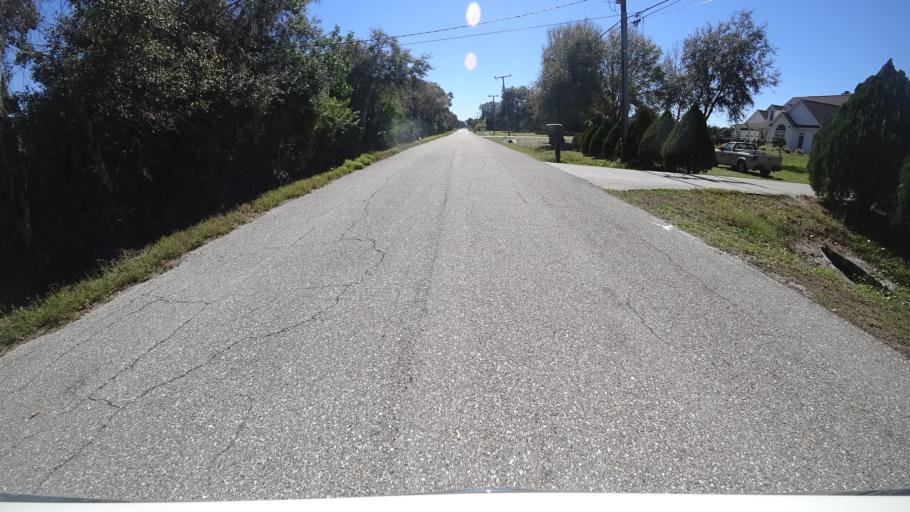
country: US
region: Florida
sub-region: Manatee County
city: Memphis
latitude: 27.5713
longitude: -82.5483
